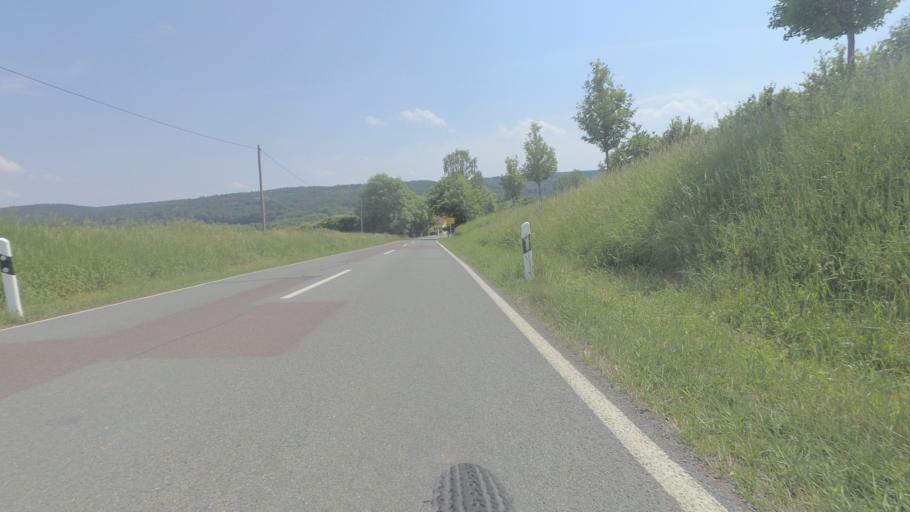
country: DE
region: Saxony-Anhalt
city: Ballenstedt
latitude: 51.7062
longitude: 11.2855
